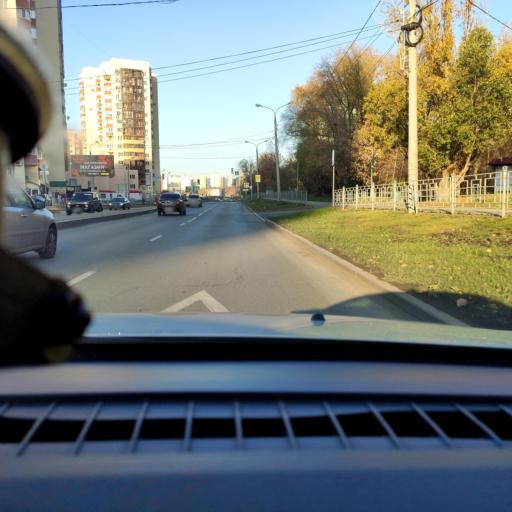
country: RU
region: Samara
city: Samara
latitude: 53.2422
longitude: 50.1895
